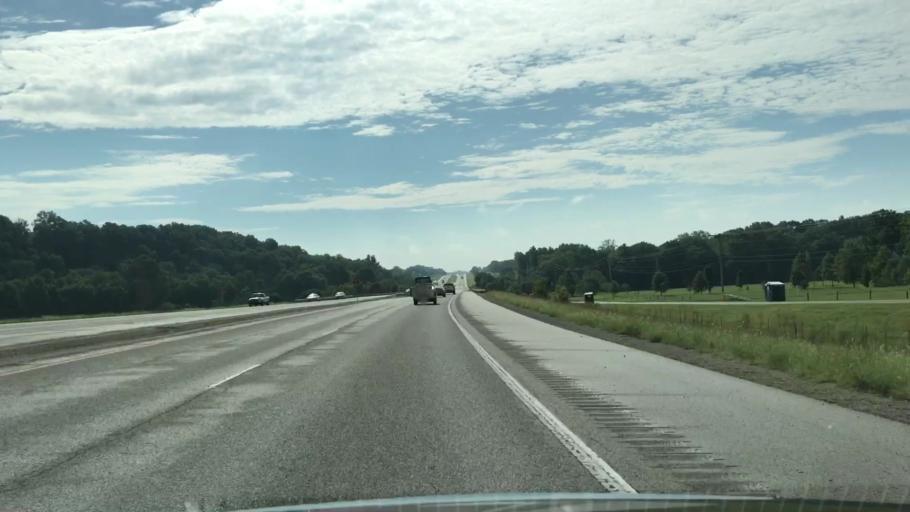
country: US
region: Kentucky
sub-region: Warren County
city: Plano
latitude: 36.8989
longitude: -86.3853
